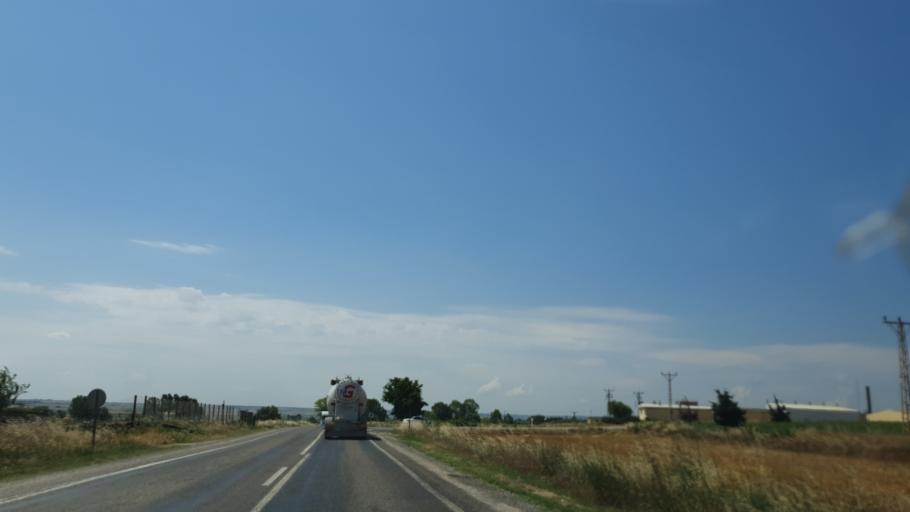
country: TR
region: Tekirdag
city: Saray
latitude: 41.5204
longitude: 27.8555
